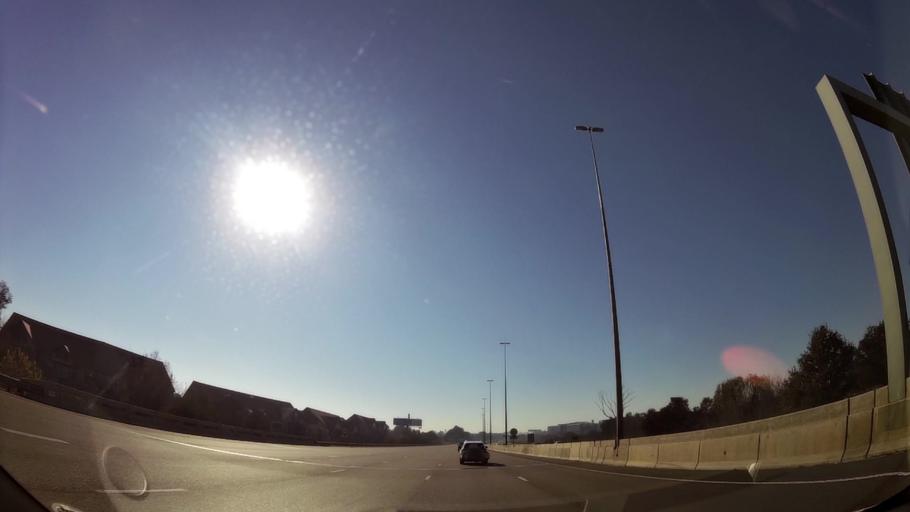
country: ZA
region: Gauteng
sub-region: City of Tshwane Metropolitan Municipality
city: Centurion
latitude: -25.8642
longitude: 28.1990
